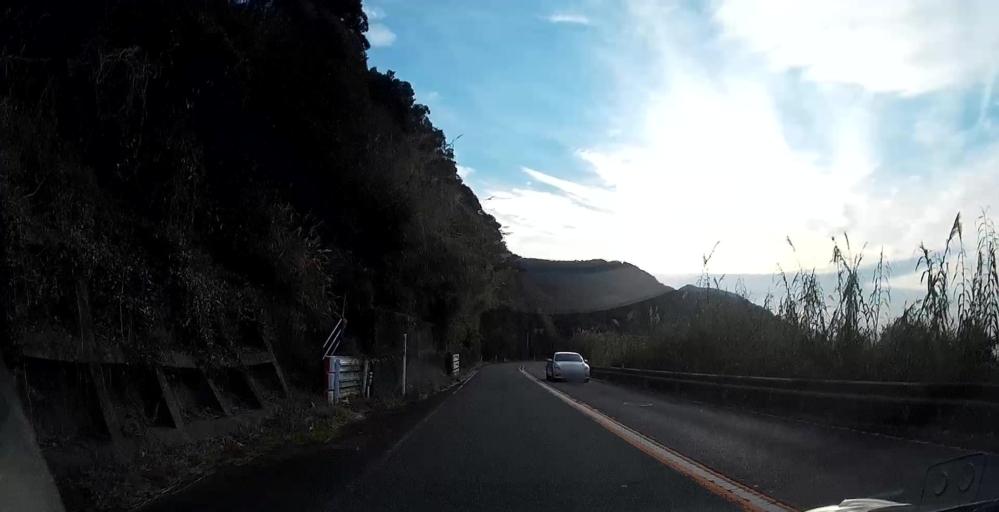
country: JP
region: Kumamoto
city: Matsubase
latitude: 32.6508
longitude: 130.4955
